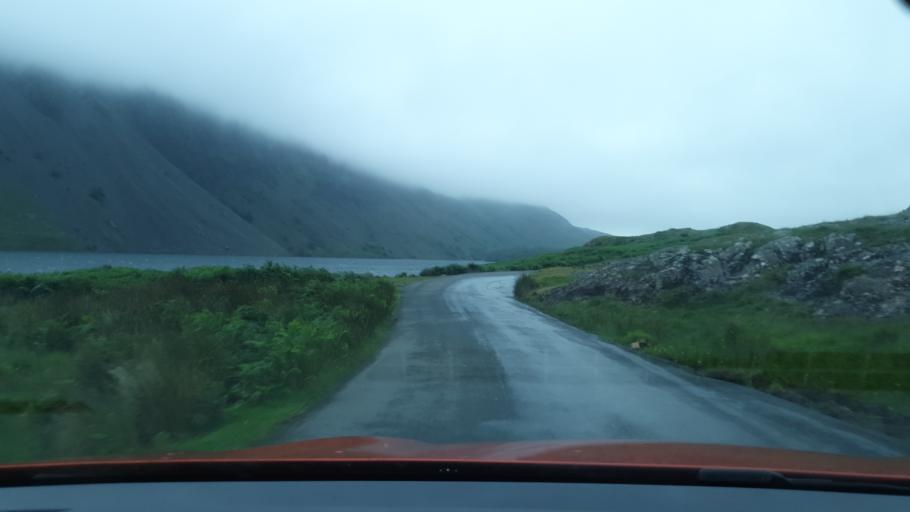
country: GB
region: England
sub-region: Cumbria
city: Seascale
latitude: 54.4390
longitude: -3.3073
